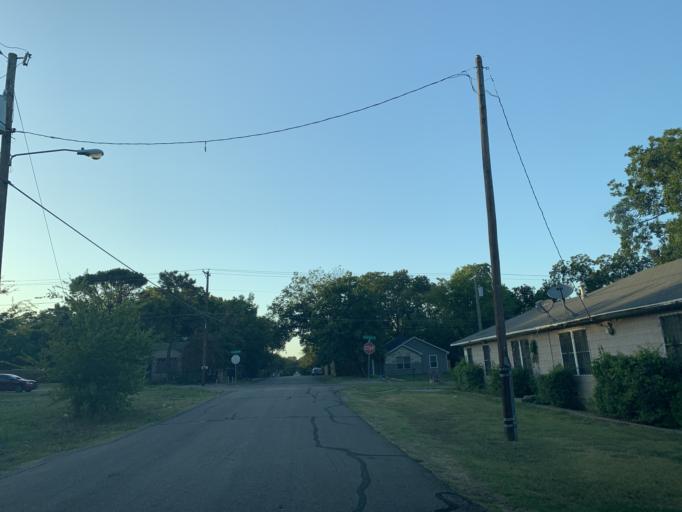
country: US
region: Texas
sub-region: Dallas County
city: Dallas
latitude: 32.7025
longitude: -96.8028
